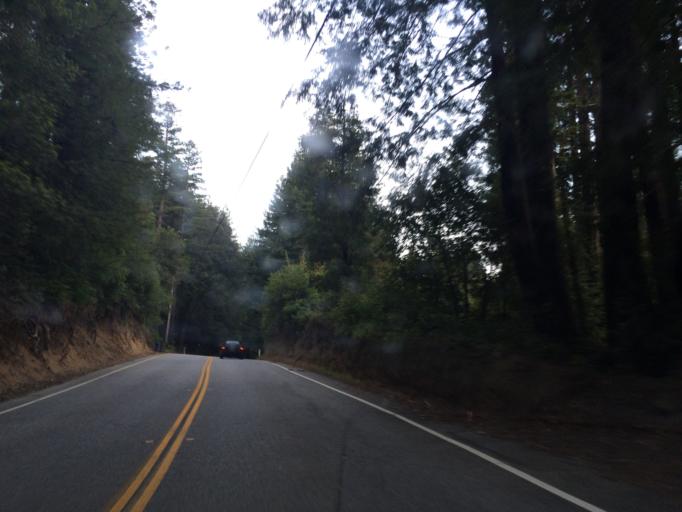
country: US
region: California
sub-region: Santa Cruz County
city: Boulder Creek
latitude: 37.1982
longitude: -122.1464
